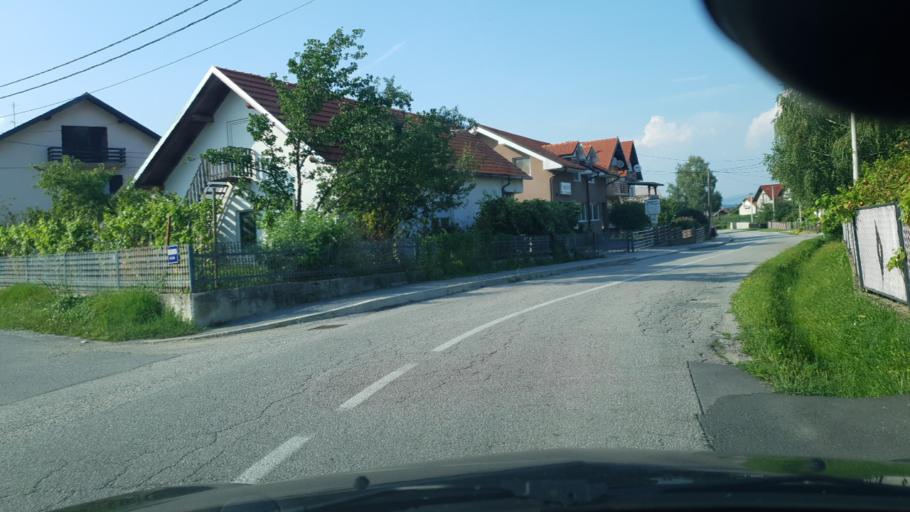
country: HR
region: Krapinsko-Zagorska
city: Oroslavje
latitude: 45.9792
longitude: 15.9212
